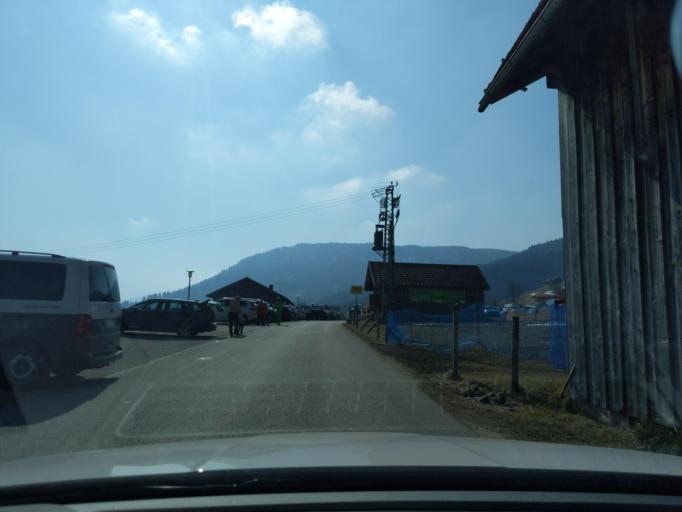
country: DE
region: Bavaria
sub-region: Swabia
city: Obermaiselstein
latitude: 47.4576
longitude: 10.2323
